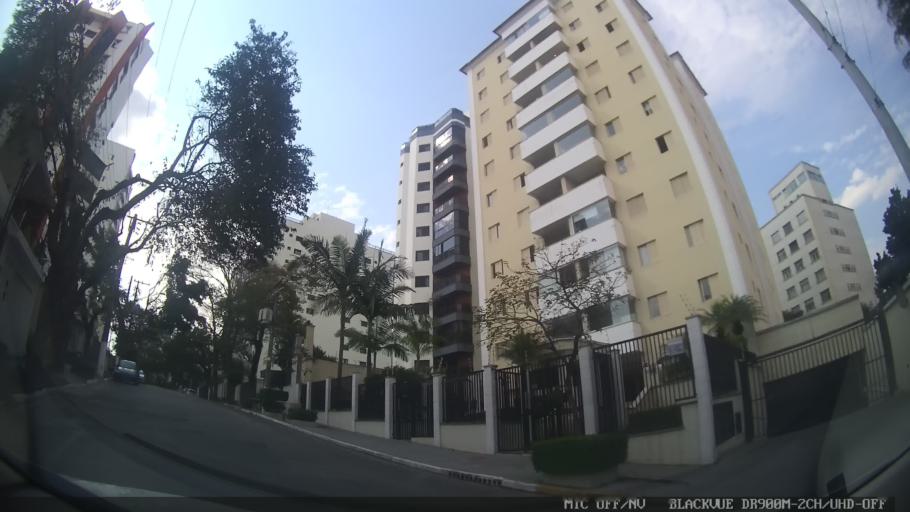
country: BR
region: Sao Paulo
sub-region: Sao Paulo
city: Sao Paulo
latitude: -23.5768
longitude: -46.6144
